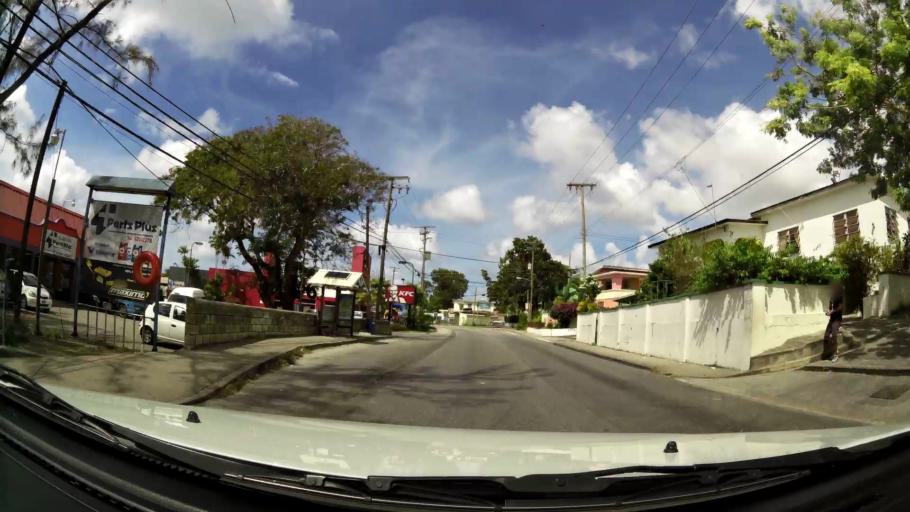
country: BB
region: Saint Michael
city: Bridgetown
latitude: 13.1270
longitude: -59.6276
